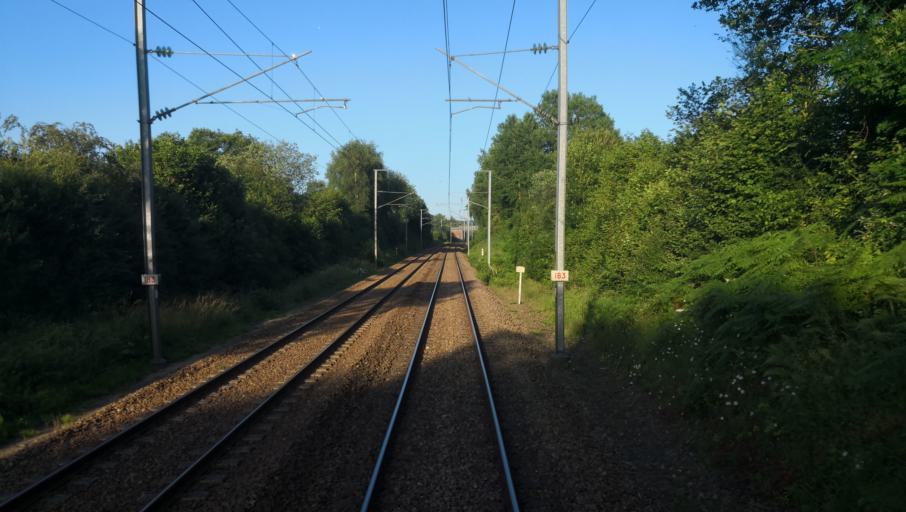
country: FR
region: Lower Normandy
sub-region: Departement du Calvados
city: Beuvillers
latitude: 49.1223
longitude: 0.3221
